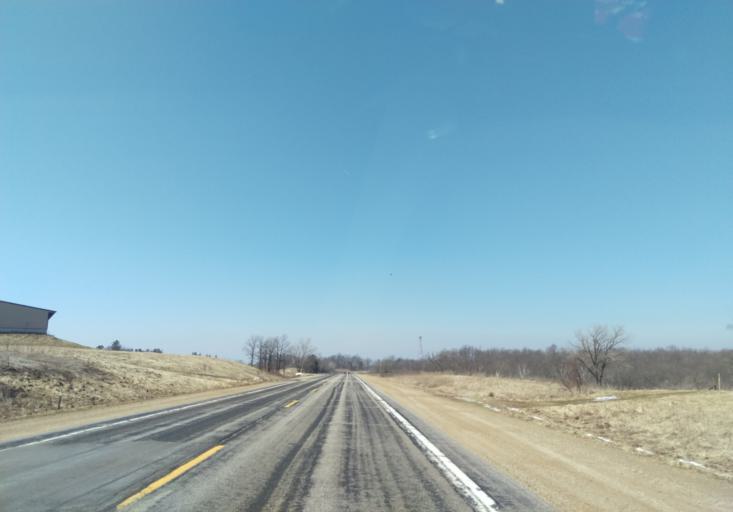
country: US
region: Wisconsin
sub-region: Vernon County
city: Westby
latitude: 43.6652
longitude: -90.9383
